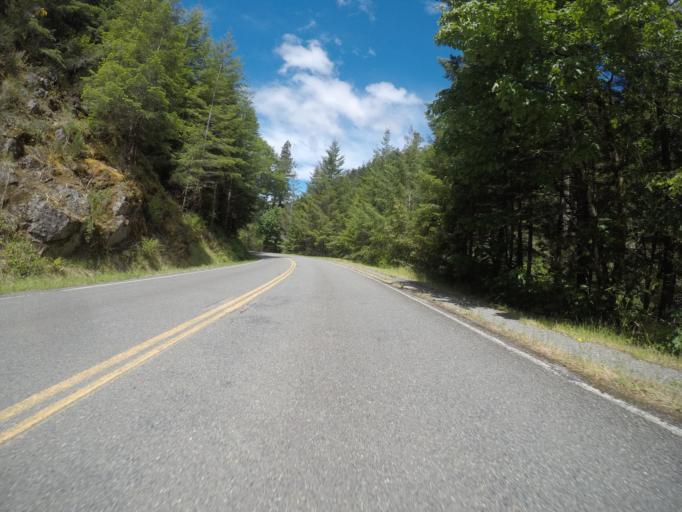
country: US
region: California
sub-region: Del Norte County
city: Bertsch-Oceanview
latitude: 41.7944
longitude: -124.0355
